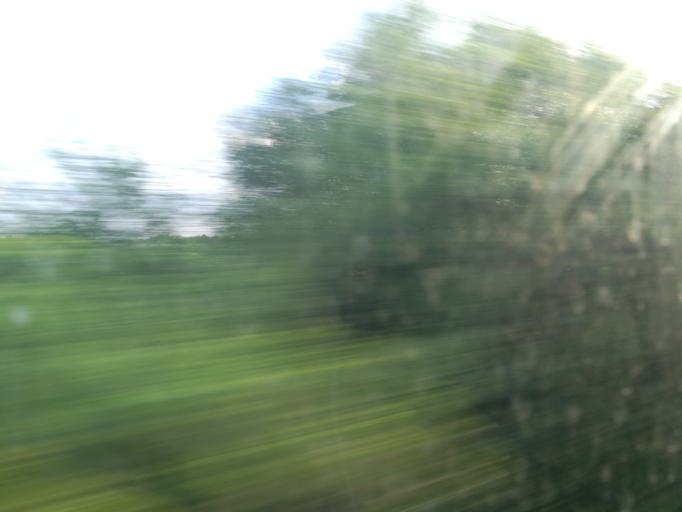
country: RO
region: Arges
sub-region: Comuna Leordeni
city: Ciulnita
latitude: 44.7781
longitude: 25.1411
